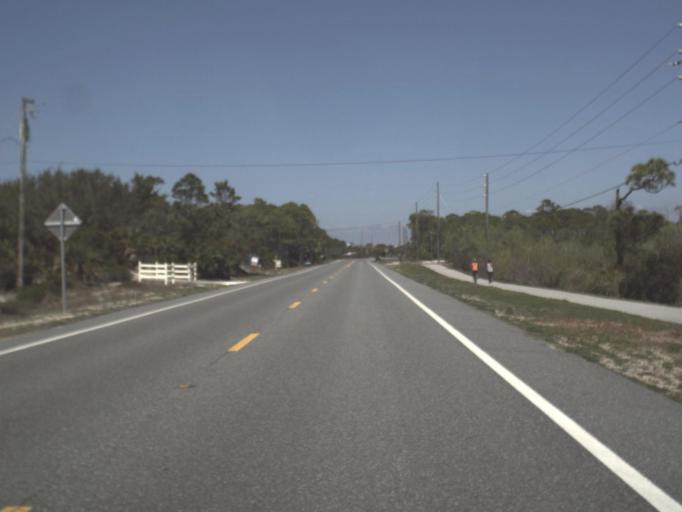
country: US
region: Florida
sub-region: Gulf County
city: Port Saint Joe
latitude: 29.7396
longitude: -85.3943
